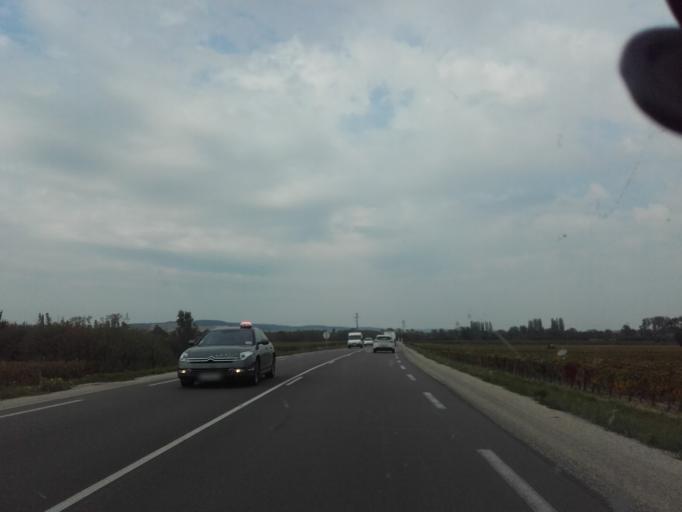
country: FR
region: Bourgogne
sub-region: Departement de la Cote-d'Or
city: Corpeau
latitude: 46.9521
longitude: 4.7649
